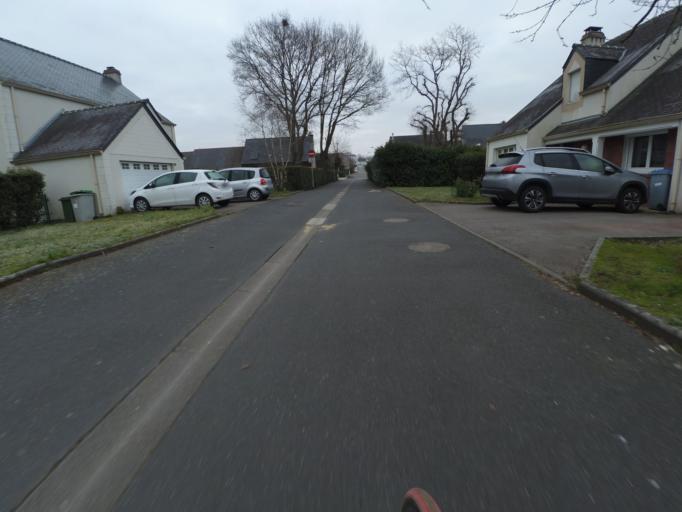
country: FR
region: Pays de la Loire
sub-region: Departement de la Loire-Atlantique
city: Carquefou
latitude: 47.3034
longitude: -1.4899
